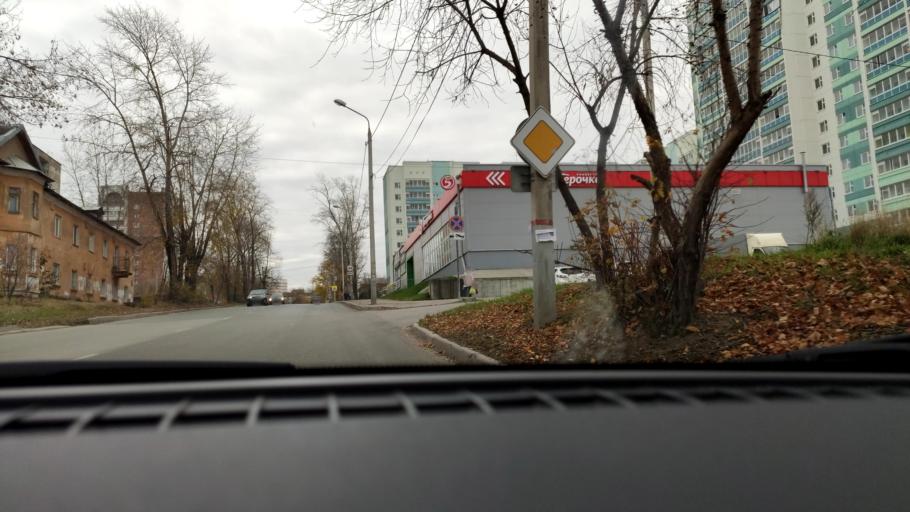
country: RU
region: Perm
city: Perm
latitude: 58.0691
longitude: 56.3545
